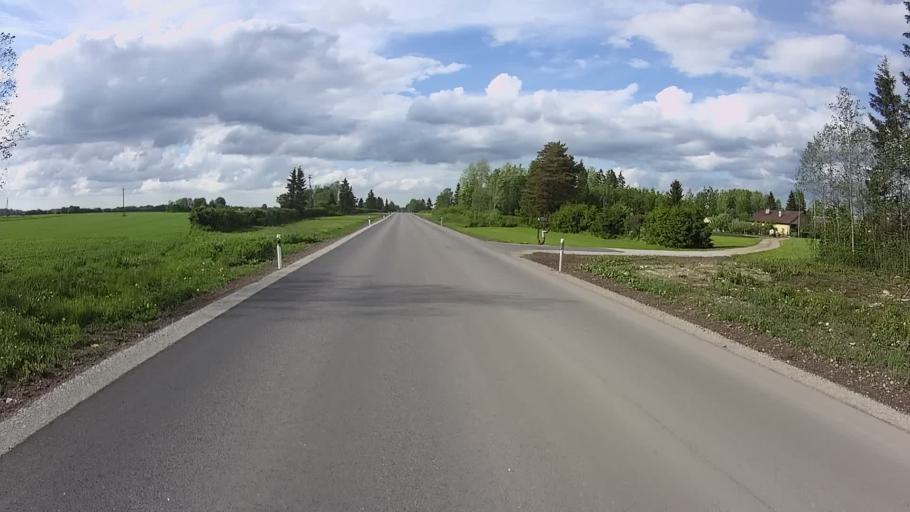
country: EE
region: Laeaene-Virumaa
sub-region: Vinni vald
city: Vinni
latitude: 59.0671
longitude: 26.6379
